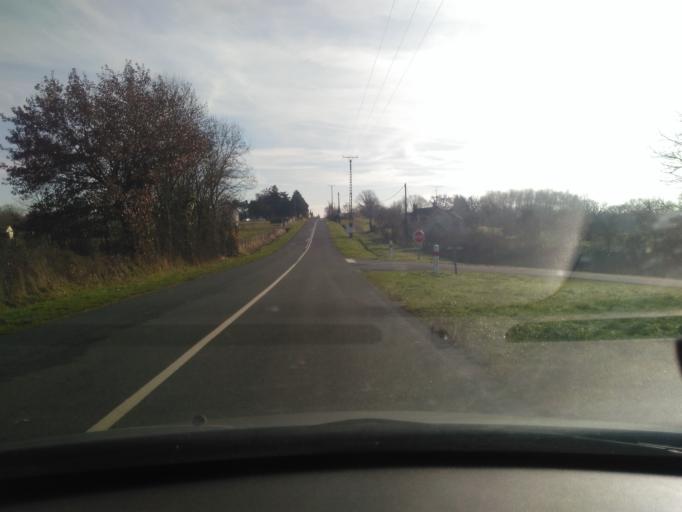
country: FR
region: Centre
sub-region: Departement du Cher
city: Chateaumeillant
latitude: 46.6324
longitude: 2.1328
